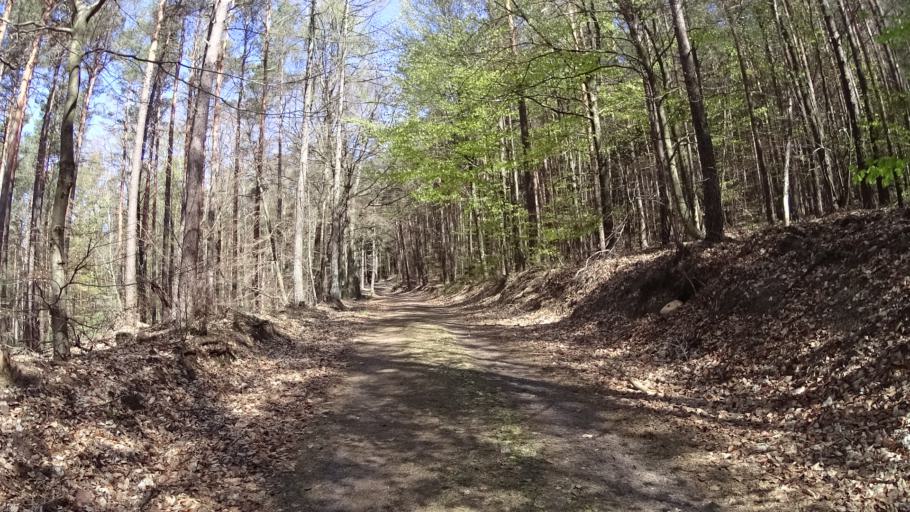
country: DE
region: Rheinland-Pfalz
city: Neidenfels
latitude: 49.3965
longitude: 8.0669
